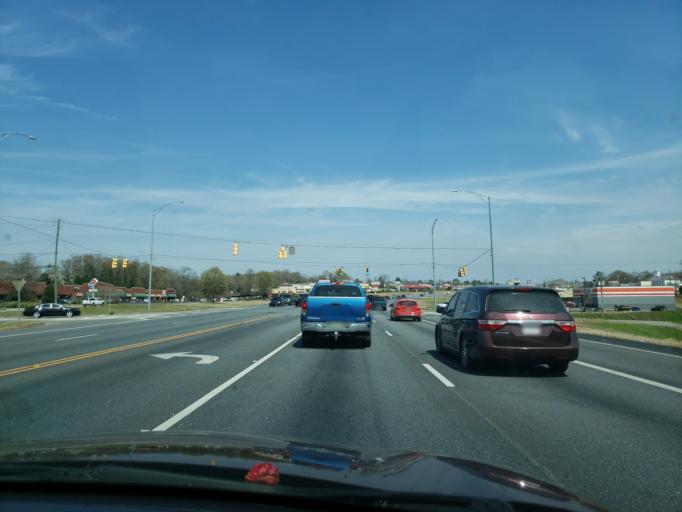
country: US
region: Alabama
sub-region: Elmore County
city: Millbrook
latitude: 32.5133
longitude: -86.3794
